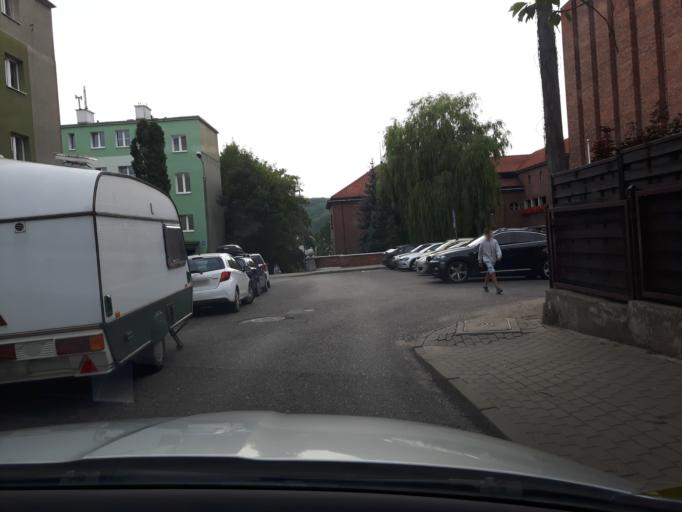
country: PL
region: Pomeranian Voivodeship
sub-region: Gdynia
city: Gdynia
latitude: 54.5064
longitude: 18.5407
